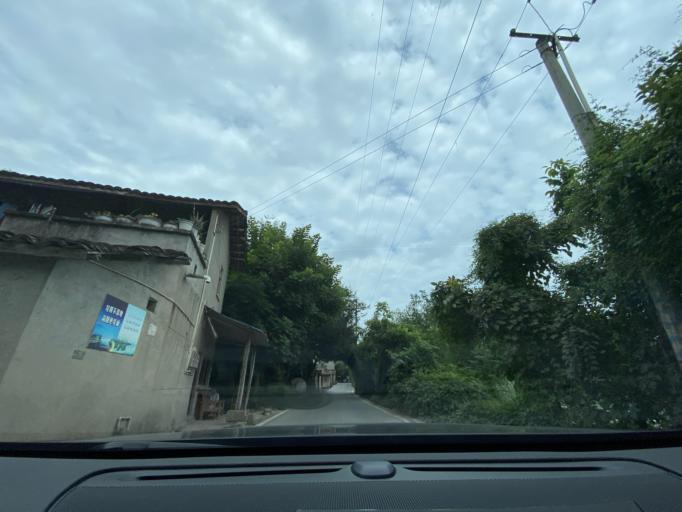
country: CN
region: Sichuan
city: Jiancheng
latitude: 30.4345
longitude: 104.5256
